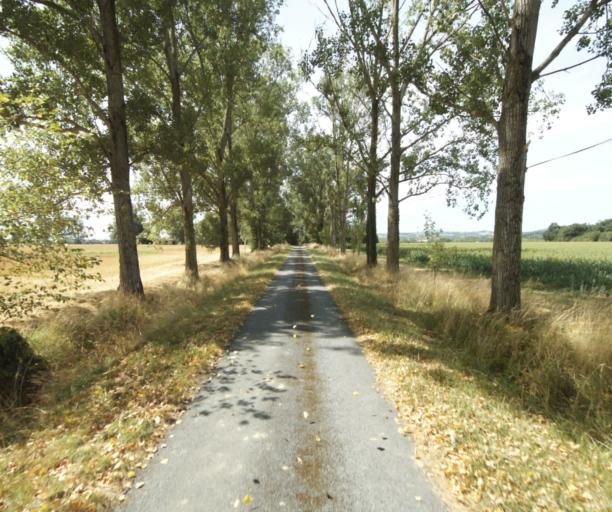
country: FR
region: Midi-Pyrenees
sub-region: Departement du Tarn
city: Soreze
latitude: 43.5064
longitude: 2.0518
